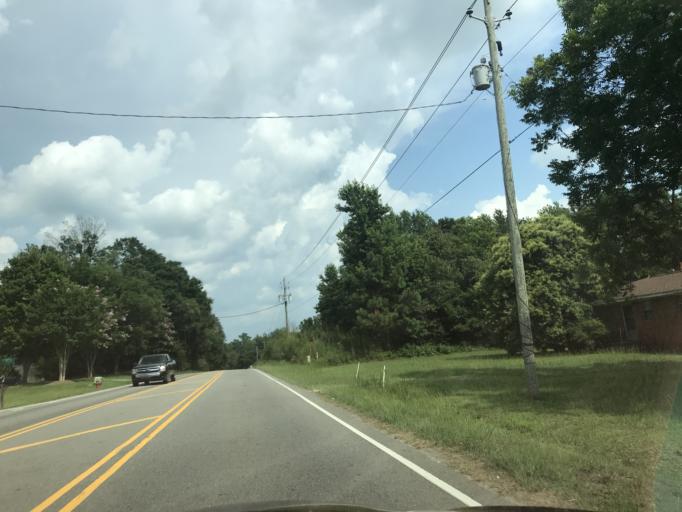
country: US
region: North Carolina
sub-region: Johnston County
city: Benson
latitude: 35.5151
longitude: -78.5503
